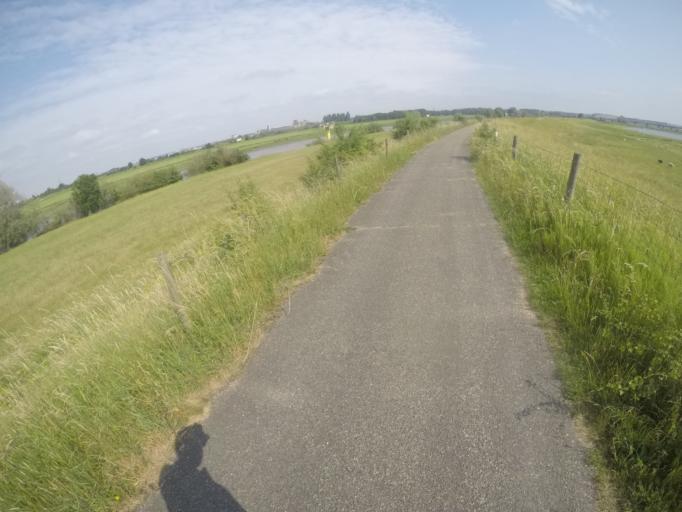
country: NL
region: Gelderland
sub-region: Gemeente Westervoort
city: Westervoort
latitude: 51.9588
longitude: 5.9511
